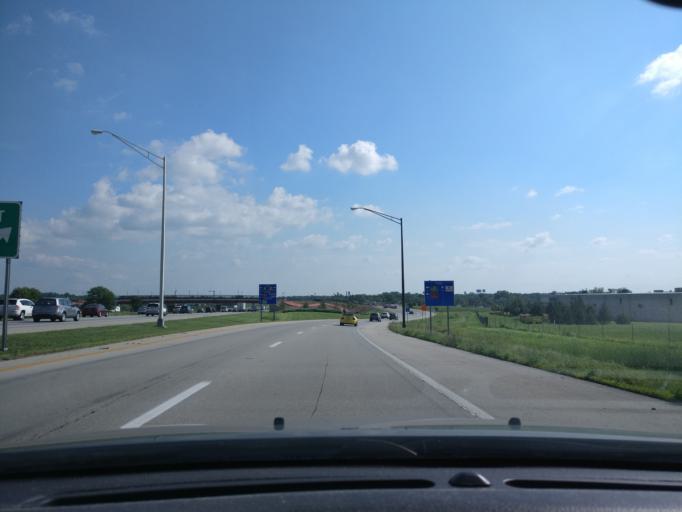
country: US
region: Ohio
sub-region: Warren County
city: Springboro
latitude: 39.6000
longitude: -84.2376
